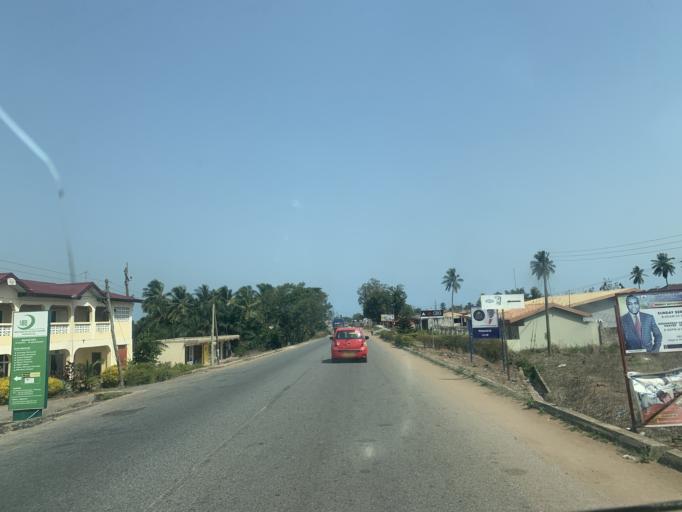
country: GH
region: Central
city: Winneba
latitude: 5.3958
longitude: -0.6486
